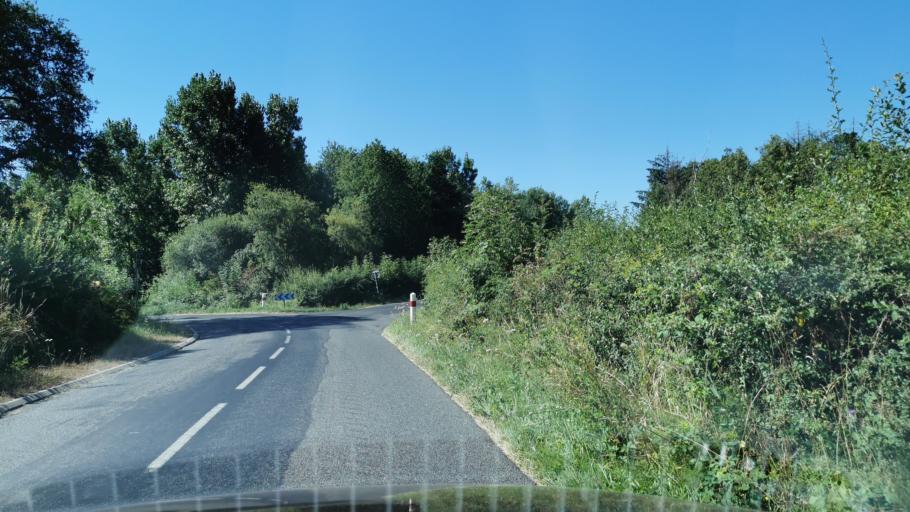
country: FR
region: Bourgogne
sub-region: Departement de Saone-et-Loire
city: Torcy
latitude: 46.7714
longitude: 4.4713
